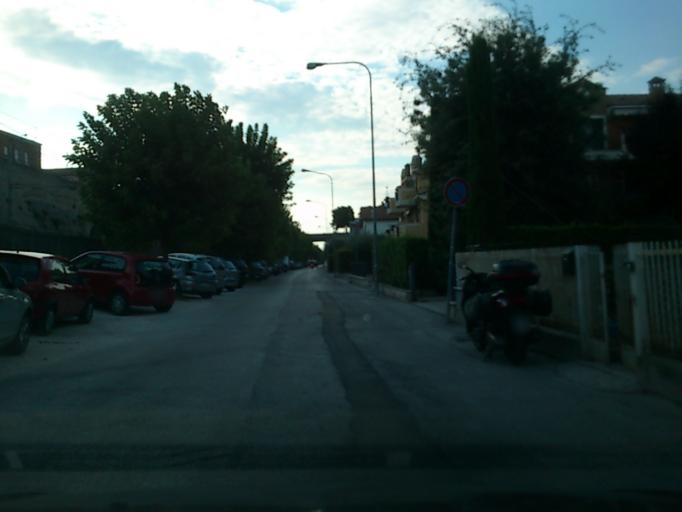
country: IT
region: The Marches
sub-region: Provincia di Pesaro e Urbino
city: Fano
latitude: 43.8451
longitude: 13.0201
